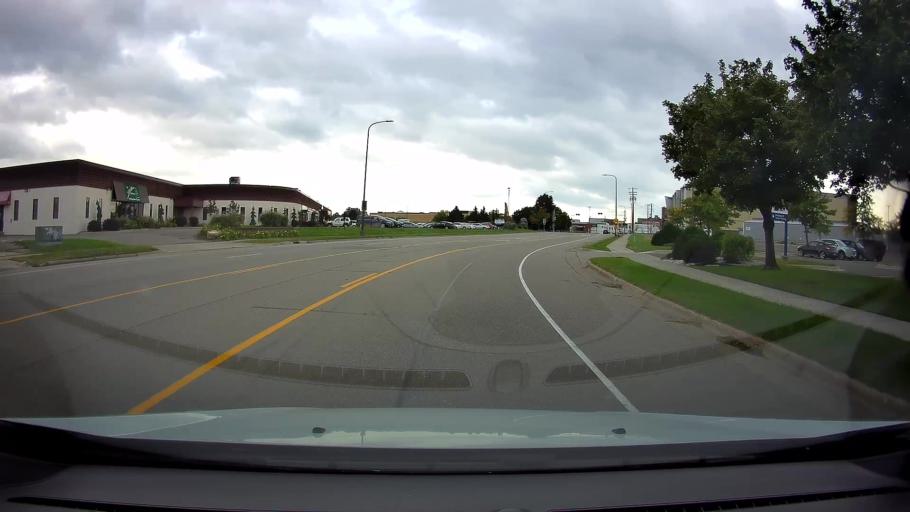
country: US
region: Minnesota
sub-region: Ramsey County
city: Falcon Heights
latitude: 44.9620
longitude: -93.1861
